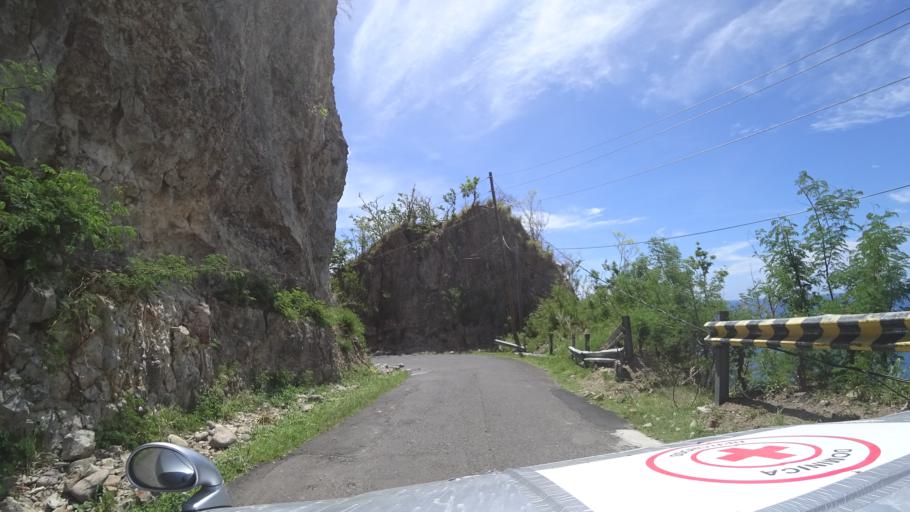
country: DM
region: Saint Mark
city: Soufriere
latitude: 15.2427
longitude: -61.3721
